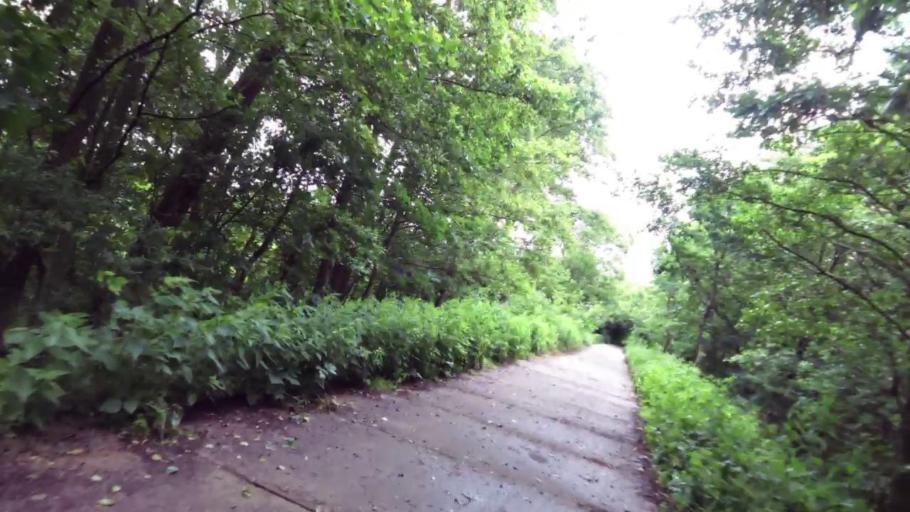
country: PL
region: West Pomeranian Voivodeship
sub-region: Powiat slawienski
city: Darlowo
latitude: 54.4914
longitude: 16.4406
